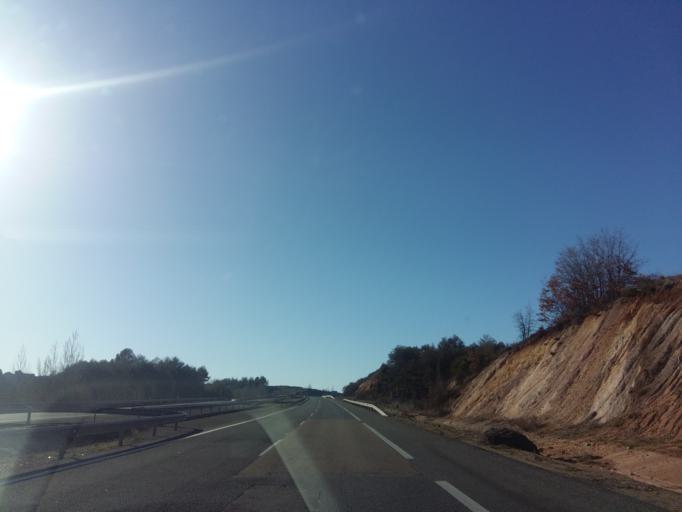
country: ES
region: Castille and Leon
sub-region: Provincia de Palencia
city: Aguilar de Campoo
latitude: 42.7349
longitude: -4.2889
